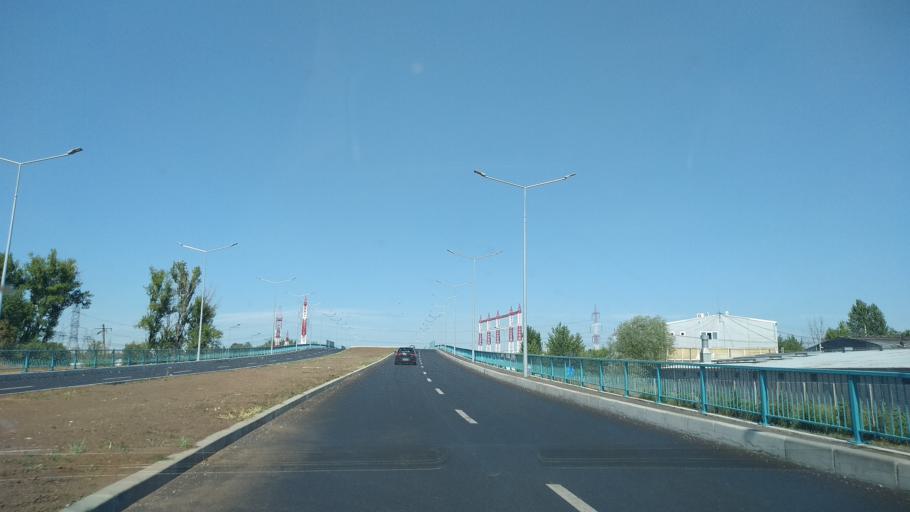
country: RO
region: Ilfov
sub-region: Comuna Popesti-Leordeni
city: Popesti-Leordeni
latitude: 44.3970
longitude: 26.1587
